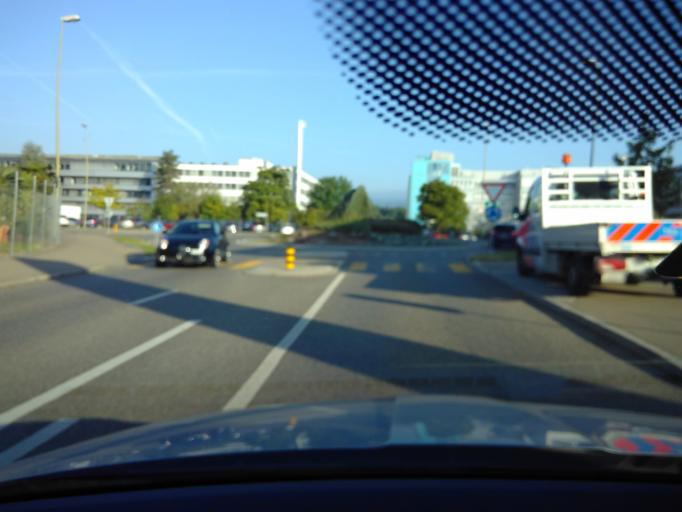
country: CH
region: Zurich
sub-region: Bezirk Dielsdorf
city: Regensdorf
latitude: 47.4380
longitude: 8.4730
